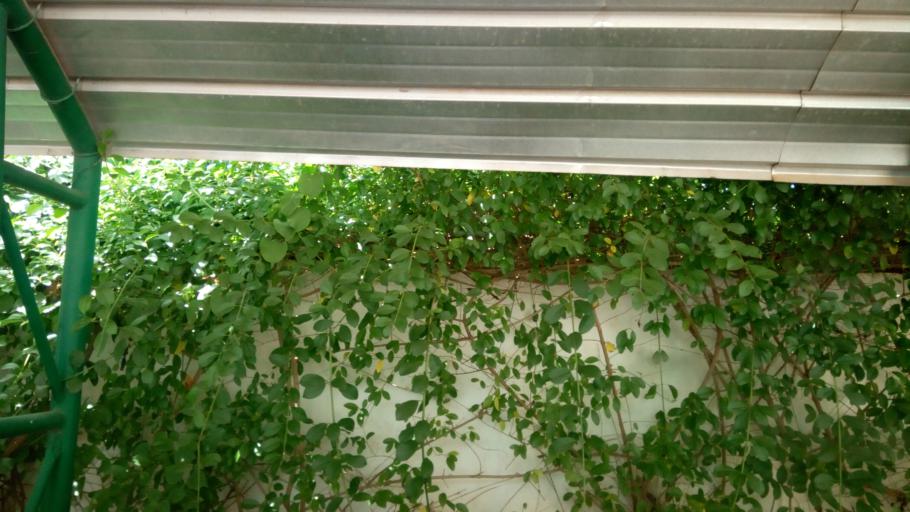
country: ML
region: Sikasso
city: Koutiala
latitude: 12.4141
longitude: -5.4703
